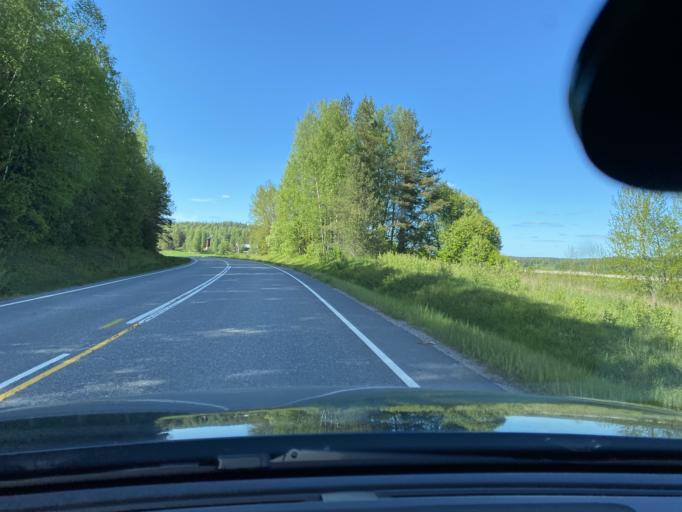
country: FI
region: Varsinais-Suomi
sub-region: Turku
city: Sauvo
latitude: 60.3745
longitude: 22.6704
